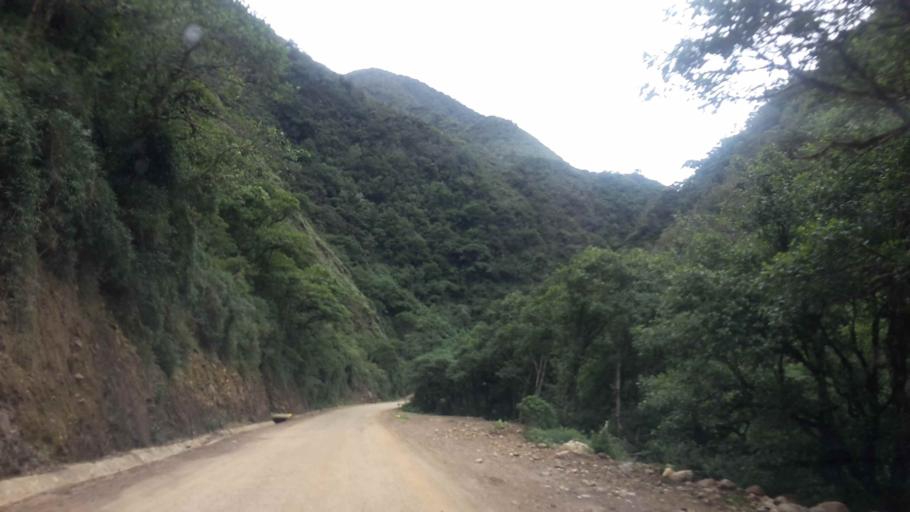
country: BO
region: Cochabamba
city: Totora
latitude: -17.5576
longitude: -65.2692
